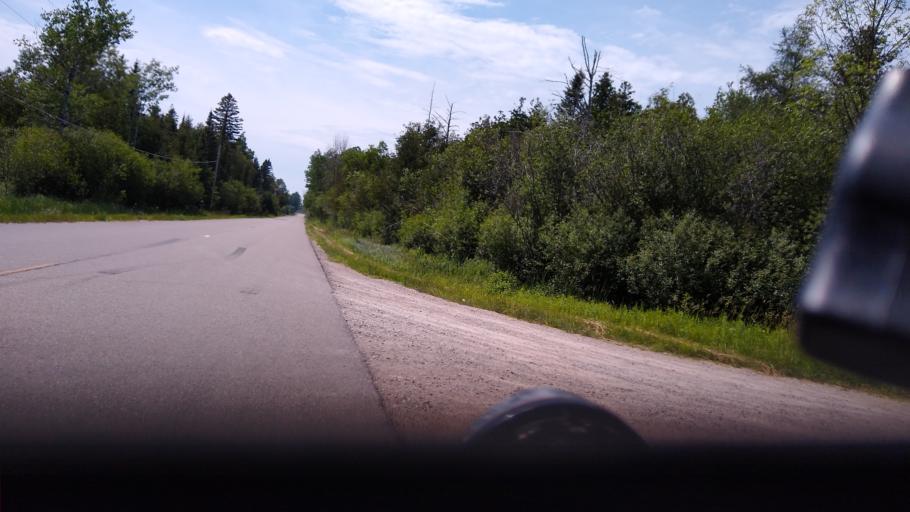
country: US
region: Michigan
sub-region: Delta County
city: Escanaba
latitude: 45.7100
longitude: -87.1113
